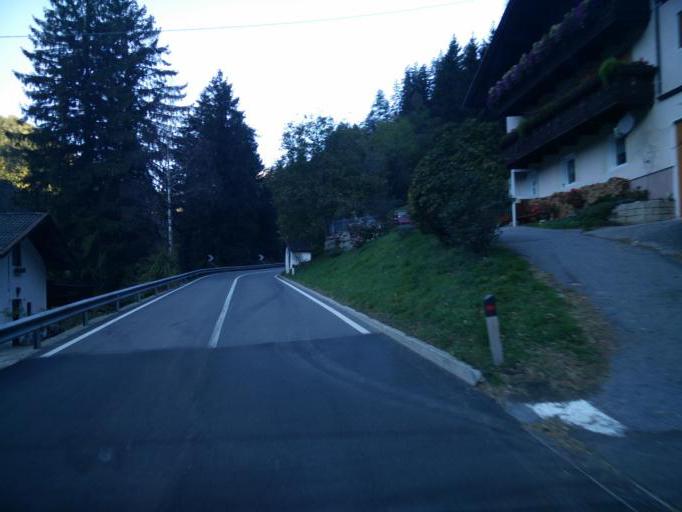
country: IT
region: Trentino-Alto Adige
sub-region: Bolzano
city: San Leonardo in Passiria
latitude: 46.8175
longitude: 11.2391
